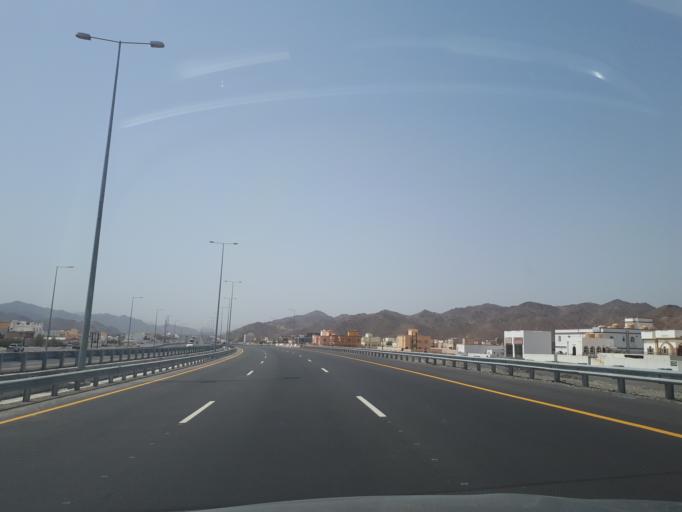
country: OM
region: Muhafazat ad Dakhiliyah
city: Bidbid
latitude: 23.4021
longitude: 58.0980
